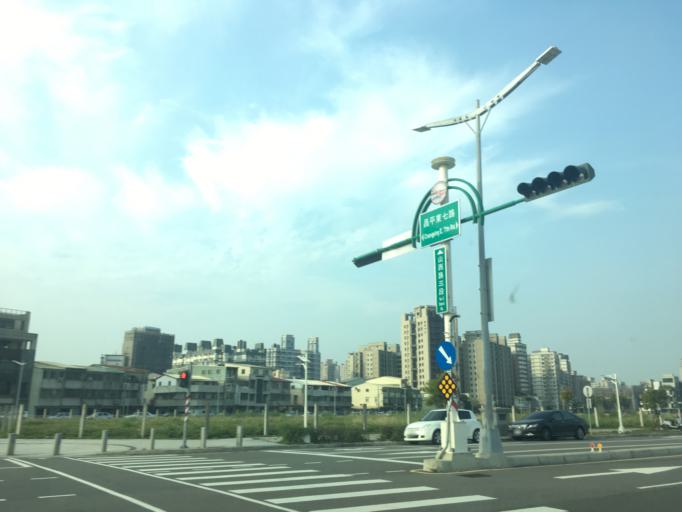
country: TW
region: Taiwan
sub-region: Taichung City
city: Taichung
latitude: 24.1856
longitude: 120.6935
